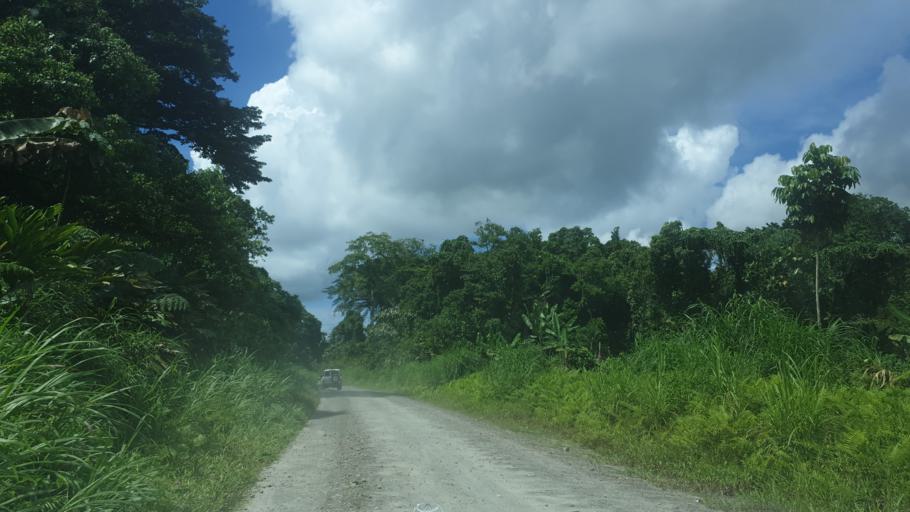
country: PG
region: Bougainville
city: Panguna
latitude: -6.7352
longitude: 155.4965
